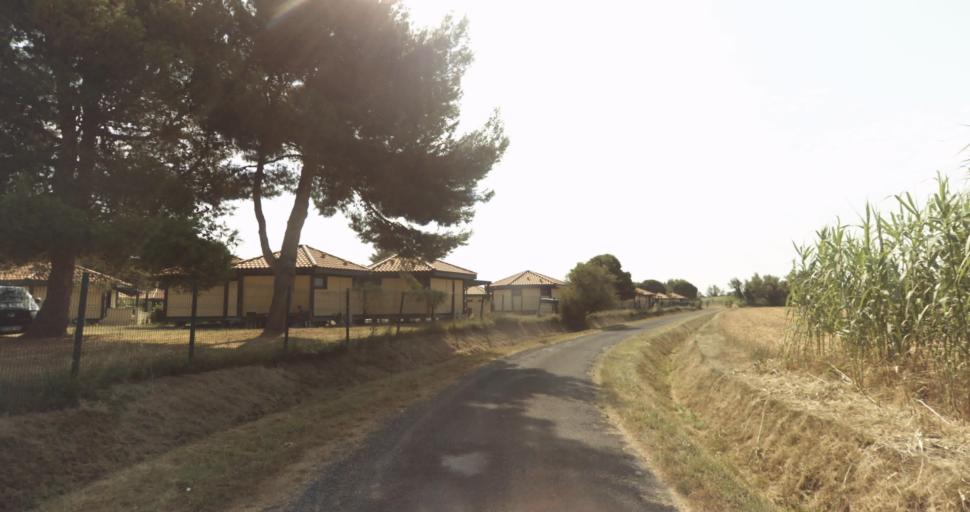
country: FR
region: Languedoc-Roussillon
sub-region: Departement des Pyrenees-Orientales
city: Latour-Bas-Elne
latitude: 42.6153
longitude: 3.0181
